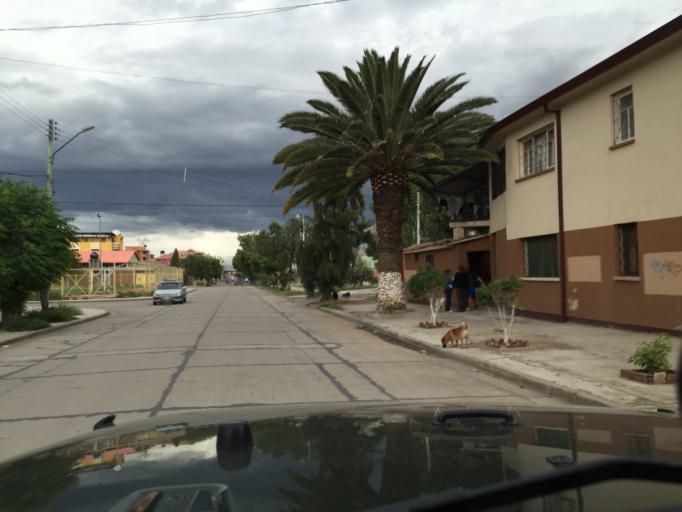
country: BO
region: Cochabamba
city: Cochabamba
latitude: -17.4173
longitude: -66.1616
